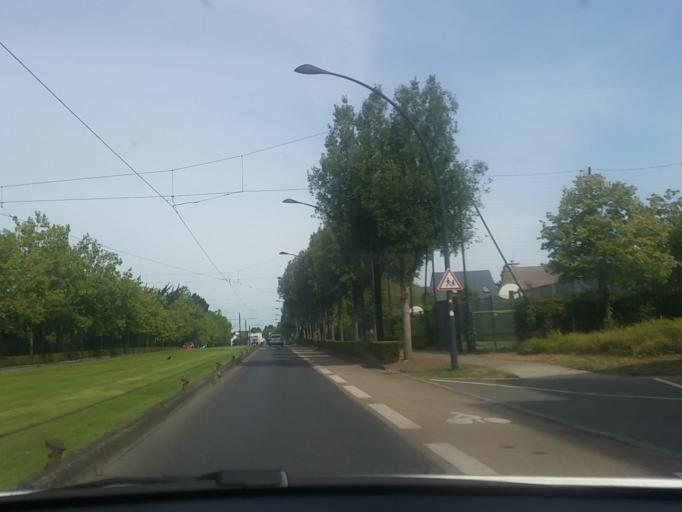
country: FR
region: Pays de la Loire
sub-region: Departement de la Loire-Atlantique
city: Bouguenais
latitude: 47.2151
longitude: -1.6087
